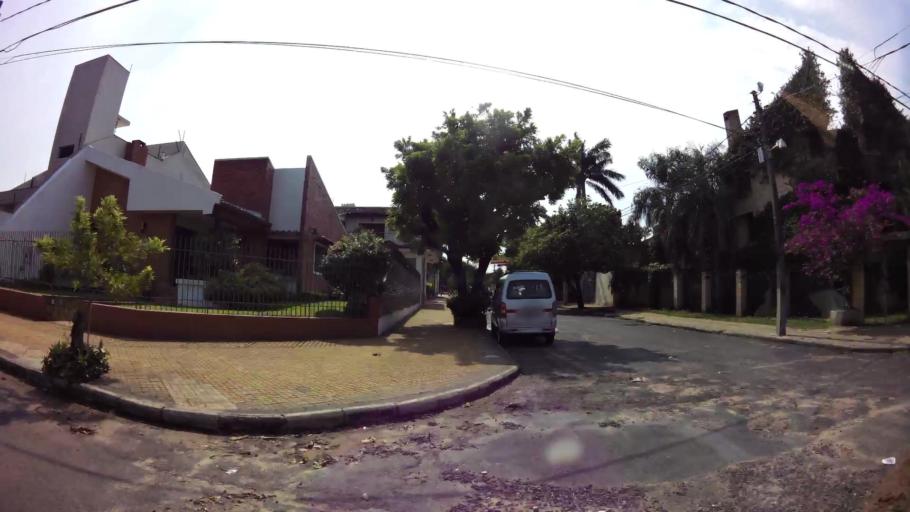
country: PY
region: Asuncion
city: Asuncion
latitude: -25.2918
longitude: -57.6554
